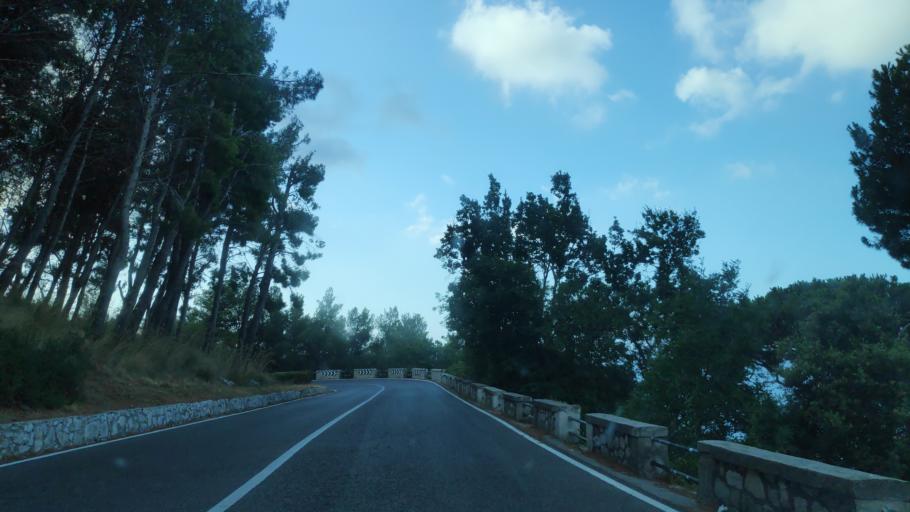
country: IT
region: Campania
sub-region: Provincia di Napoli
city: Arola-Preazzano
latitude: 40.6158
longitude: 14.4358
